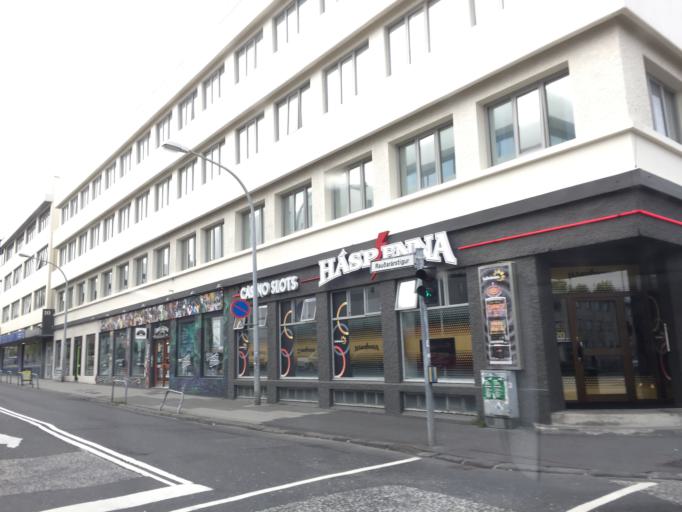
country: IS
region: Capital Region
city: Reykjavik
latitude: 64.1430
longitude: -21.9138
